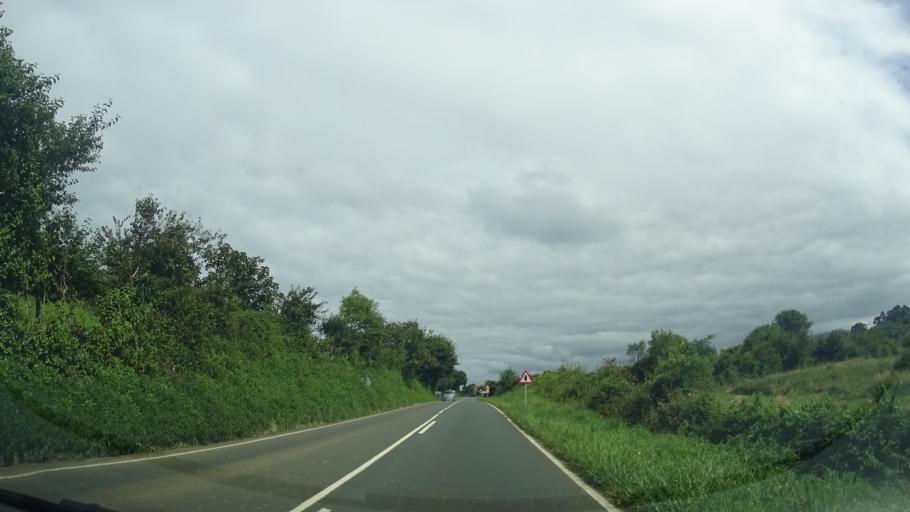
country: ES
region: Asturias
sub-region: Province of Asturias
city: Ribadesella
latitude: 43.4645
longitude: -5.1131
